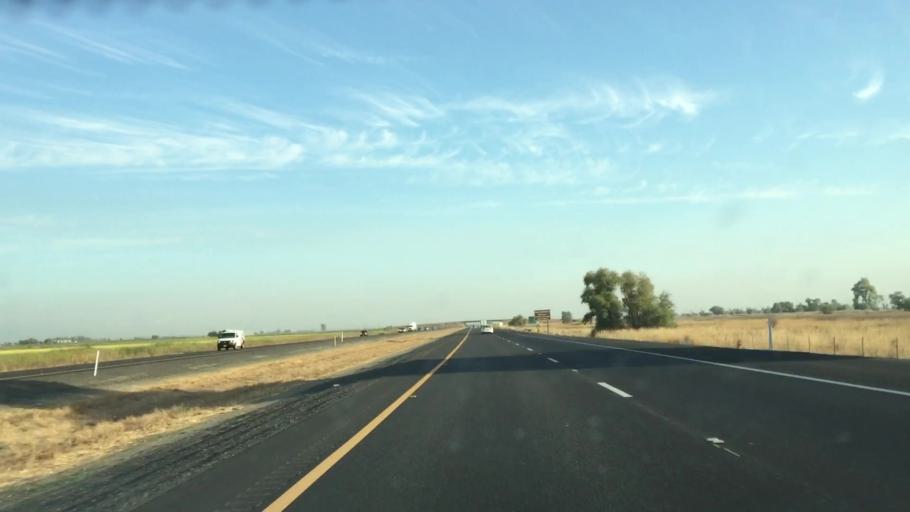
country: US
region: California
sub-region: Colusa County
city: Maxwell
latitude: 39.3985
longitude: -122.1935
